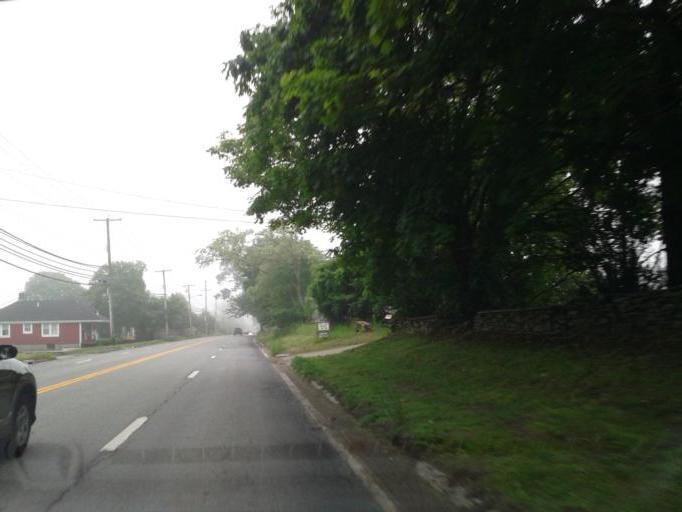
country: US
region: Rhode Island
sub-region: Newport County
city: Portsmouth
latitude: 41.5773
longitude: -71.2520
